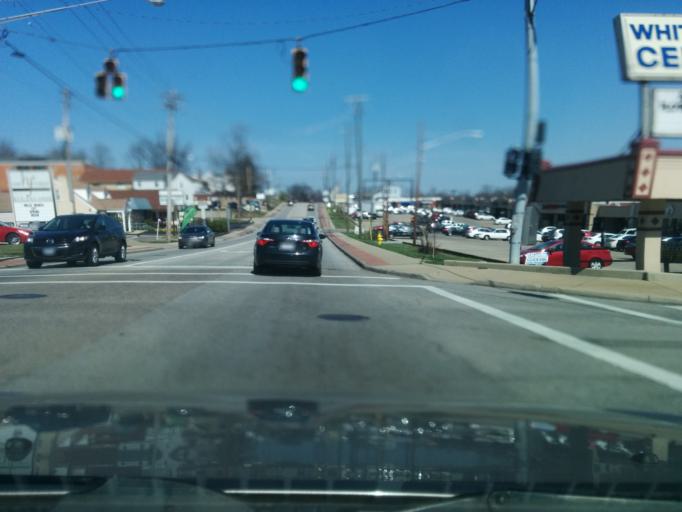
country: US
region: Ohio
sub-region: Hamilton County
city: Monfort Heights
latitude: 39.1987
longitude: -84.6010
